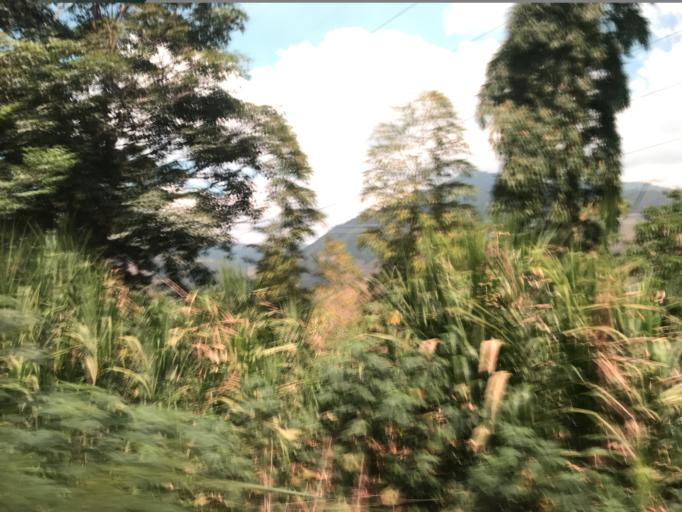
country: CO
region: Valle del Cauca
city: Cali
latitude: 3.4764
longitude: -76.5943
